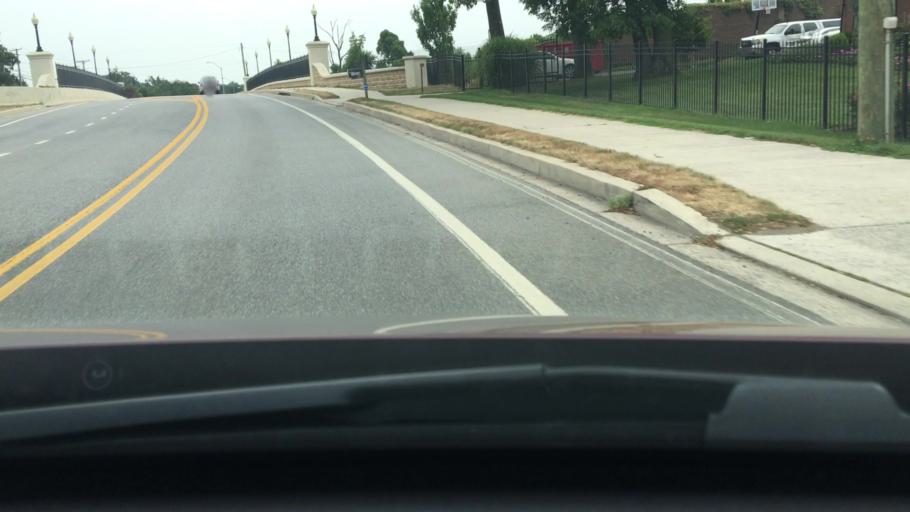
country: US
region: Maryland
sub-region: Prince George's County
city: Calverton
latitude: 39.0748
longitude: -76.9211
